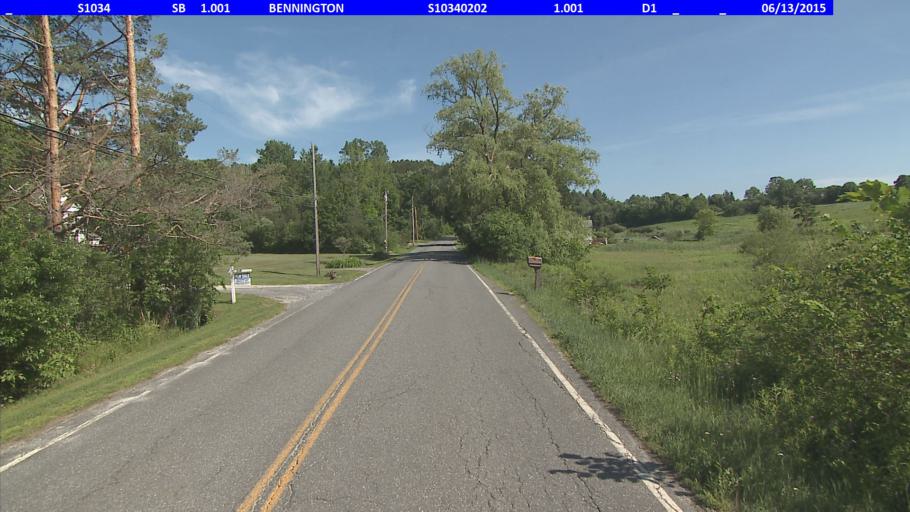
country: US
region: Vermont
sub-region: Bennington County
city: Bennington
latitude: 42.8658
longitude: -73.2089
